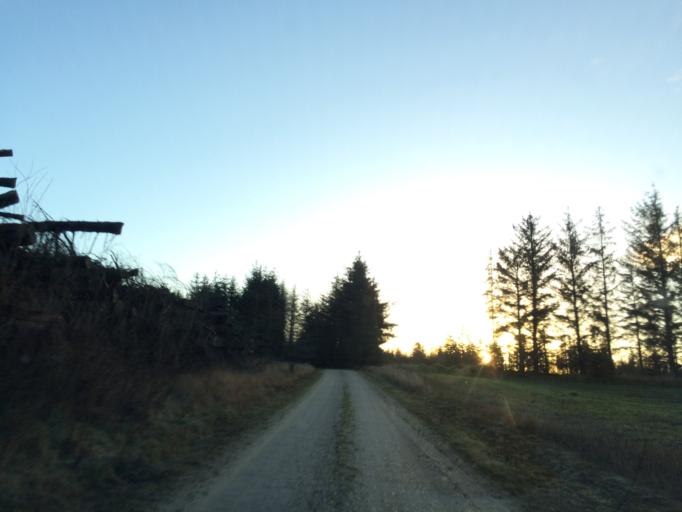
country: DK
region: Central Jutland
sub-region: Holstebro Kommune
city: Ulfborg
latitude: 56.2256
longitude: 8.4961
